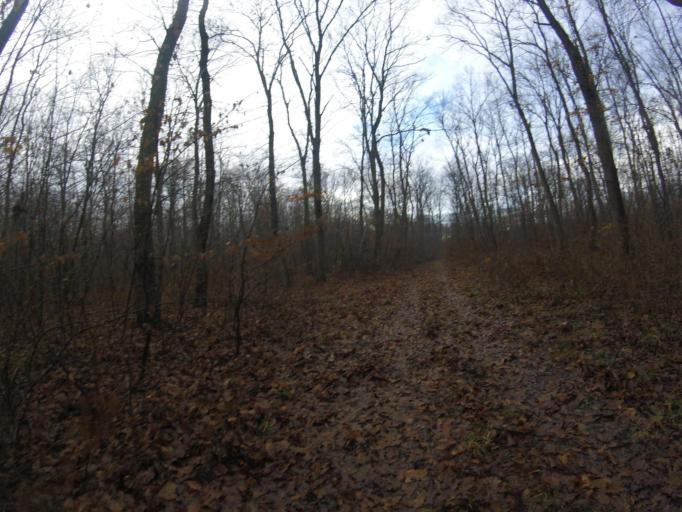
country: HU
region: Vas
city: Sarvar
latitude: 47.2402
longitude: 17.0041
